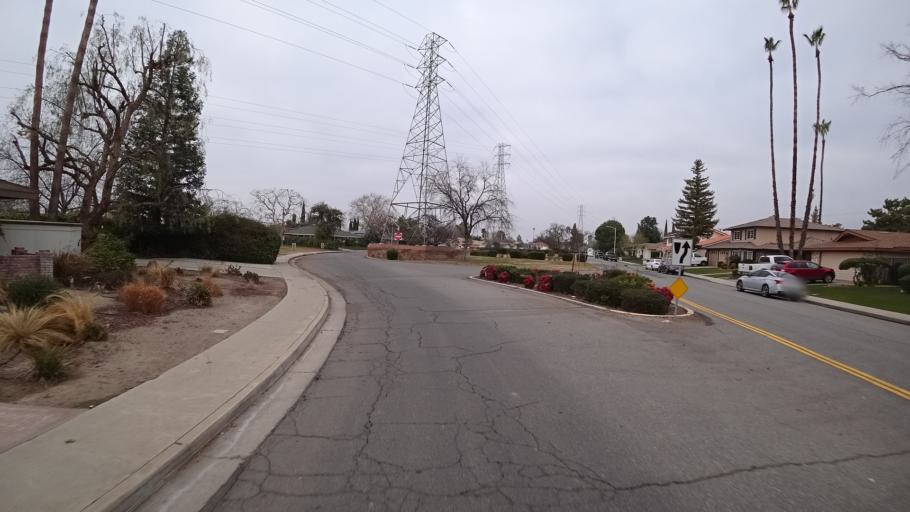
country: US
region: California
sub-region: Kern County
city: Bakersfield
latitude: 35.3859
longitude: -119.0334
